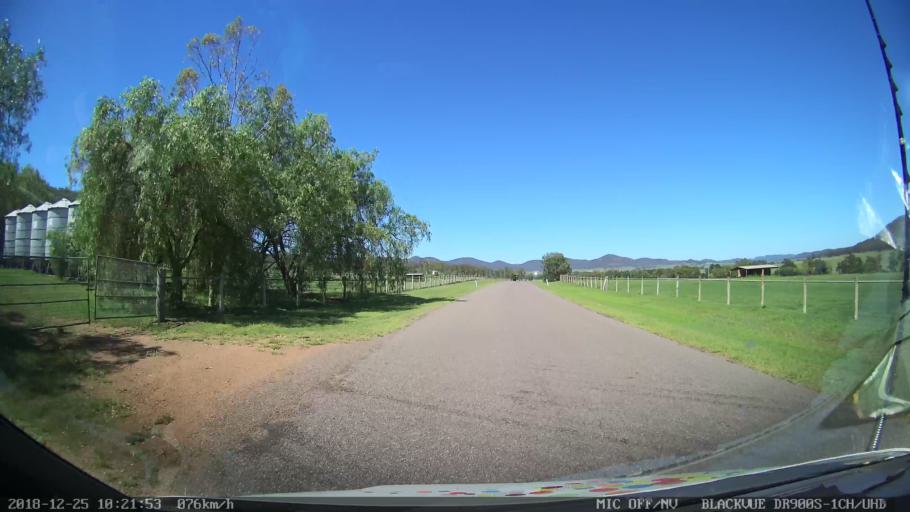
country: AU
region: New South Wales
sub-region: Muswellbrook
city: Denman
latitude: -32.3721
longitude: 150.5385
